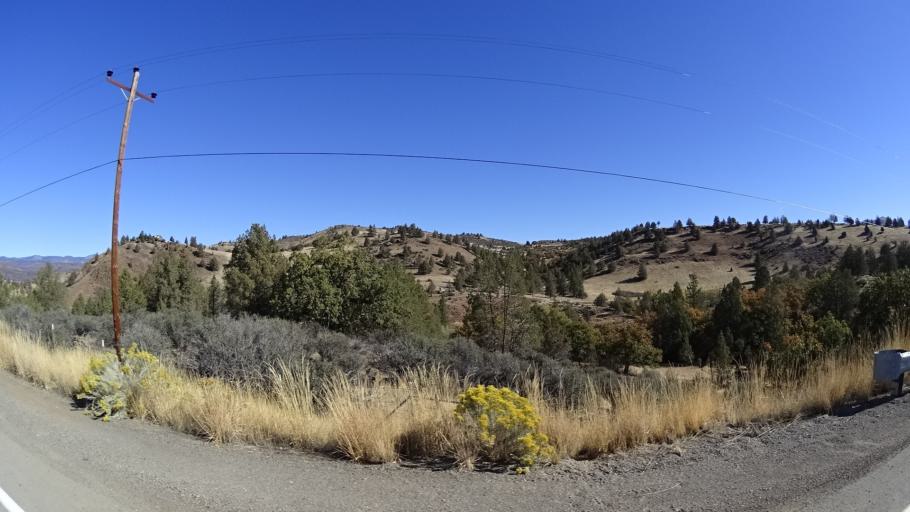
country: US
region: California
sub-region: Siskiyou County
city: Montague
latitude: 41.8715
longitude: -122.4740
